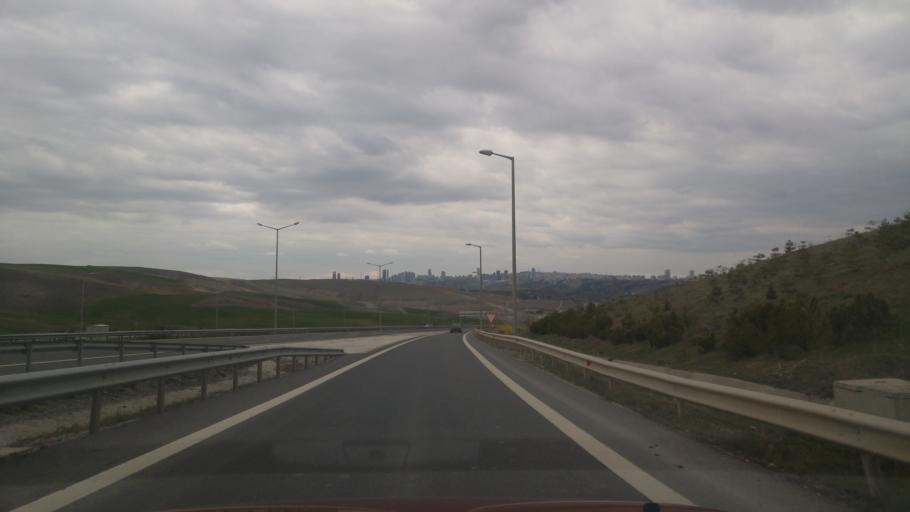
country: TR
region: Ankara
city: Mamak
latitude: 39.8729
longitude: 32.9371
